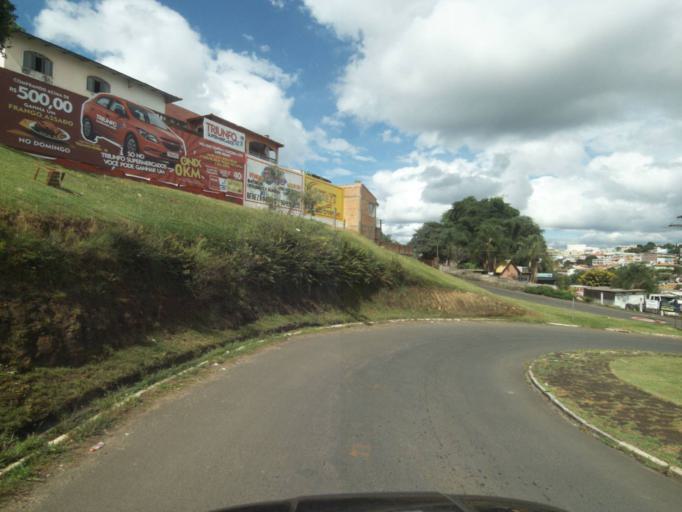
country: BR
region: Parana
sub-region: Telemaco Borba
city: Telemaco Borba
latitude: -24.3241
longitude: -50.6277
